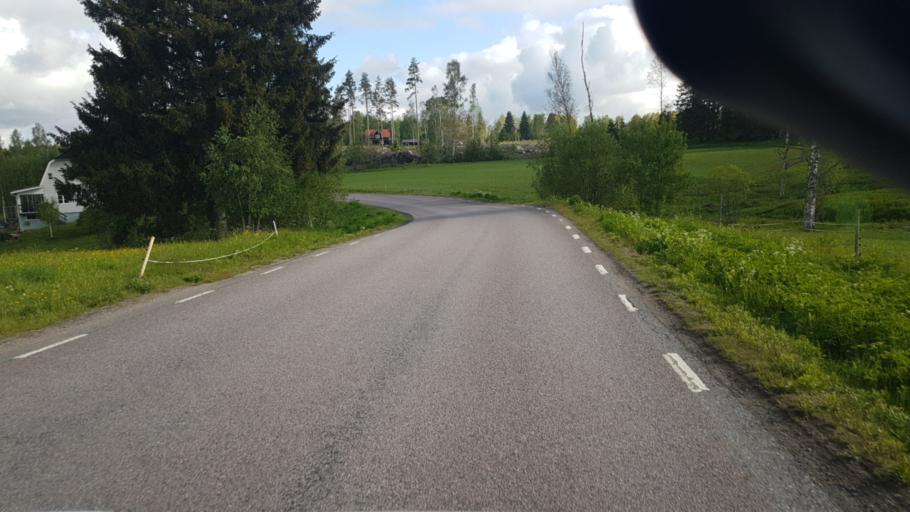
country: SE
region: Vaermland
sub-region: Eda Kommun
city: Charlottenberg
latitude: 59.7654
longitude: 12.2090
